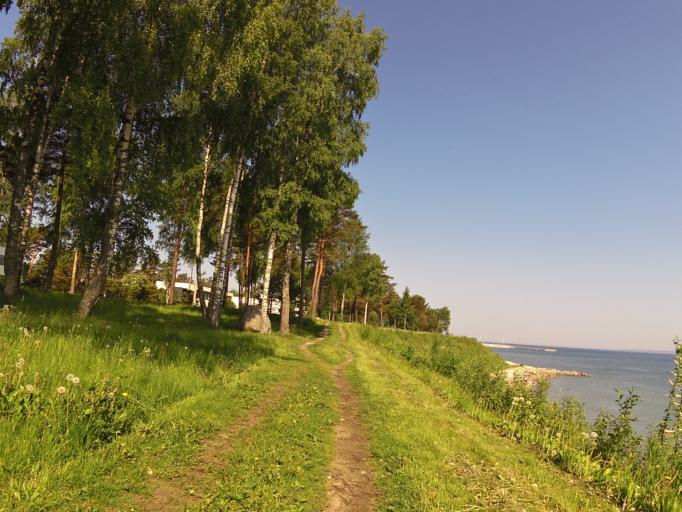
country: EE
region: Harju
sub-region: Harku vald
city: Tabasalu
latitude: 59.4453
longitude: 24.6177
